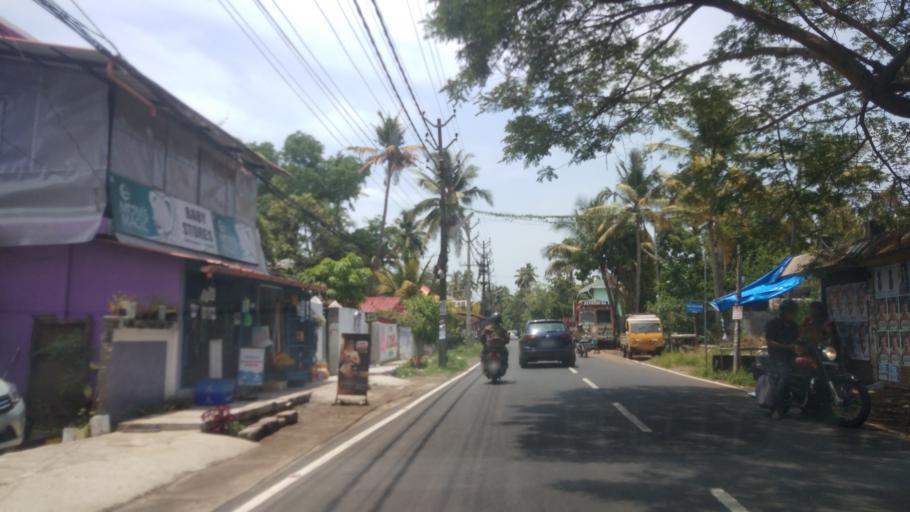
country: IN
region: Kerala
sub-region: Ernakulam
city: Cochin
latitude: 9.9010
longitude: 76.2572
